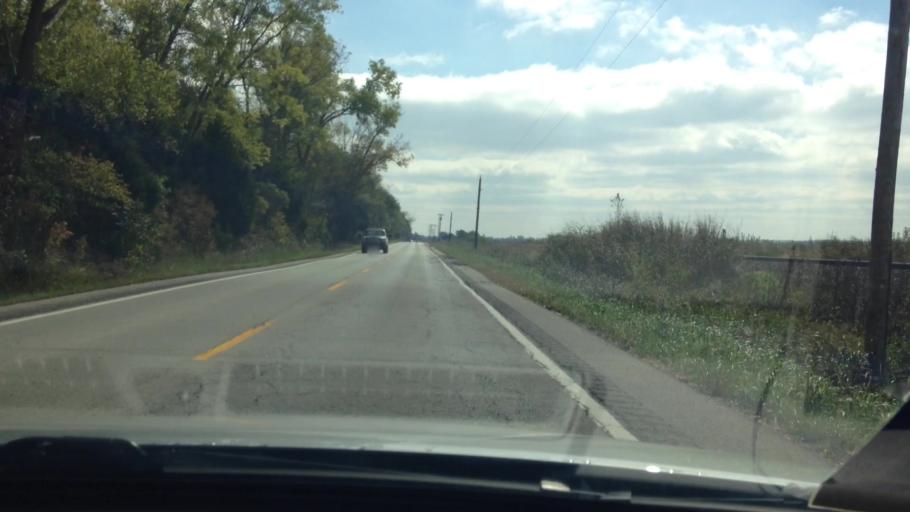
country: US
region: Kansas
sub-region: Leavenworth County
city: Lansing
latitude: 39.2960
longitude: -94.8437
